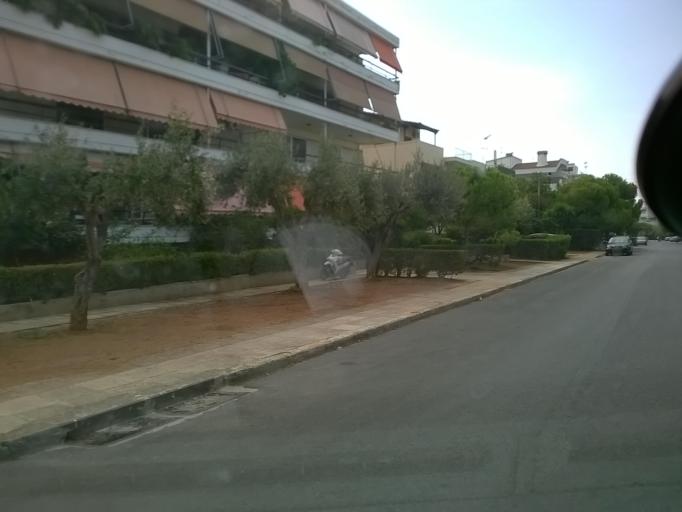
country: GR
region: Attica
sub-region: Nomarchia Athinas
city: Glyfada
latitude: 37.8627
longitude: 23.7592
